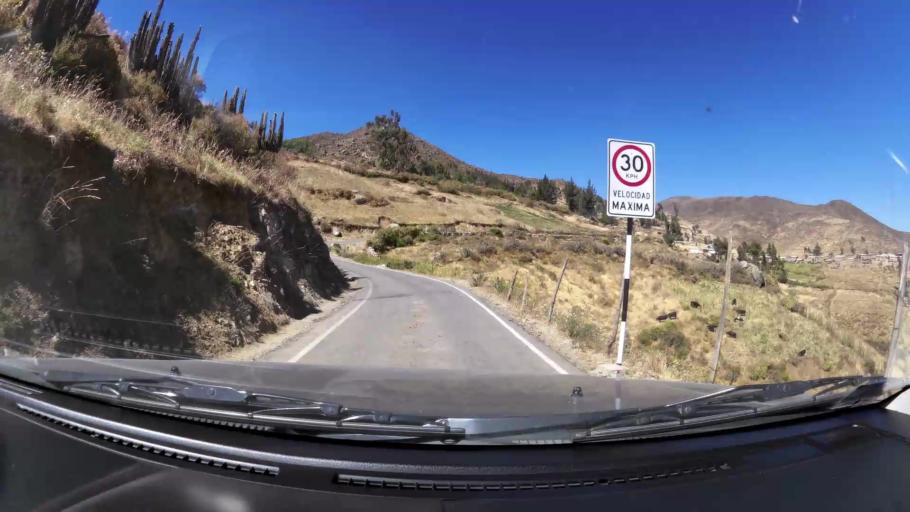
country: PE
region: Huancavelica
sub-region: Huaytara
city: Quito-Arma
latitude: -13.6828
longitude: -75.3778
